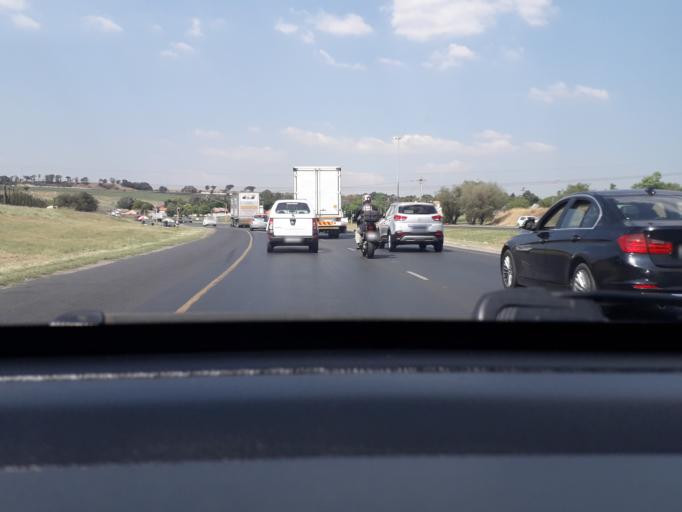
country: ZA
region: Gauteng
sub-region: City of Johannesburg Metropolitan Municipality
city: Modderfontein
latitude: -26.1016
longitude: 28.1812
